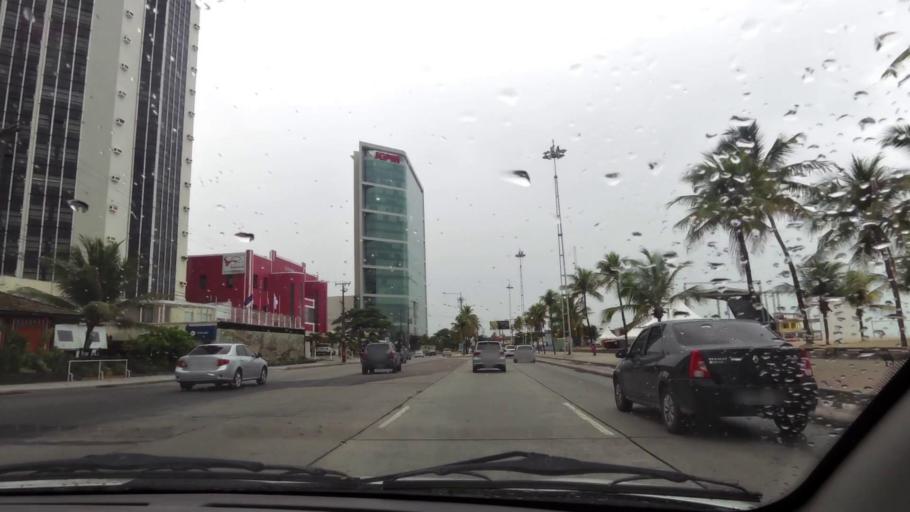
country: BR
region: Pernambuco
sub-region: Recife
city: Recife
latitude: -8.0917
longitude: -34.8820
